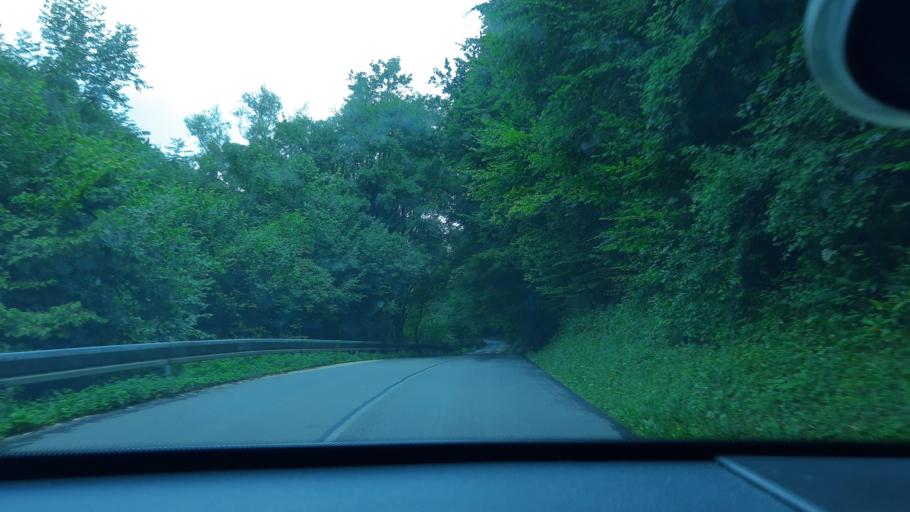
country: SK
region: Trnavsky
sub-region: Okres Trnava
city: Piestany
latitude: 48.6469
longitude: 17.9384
